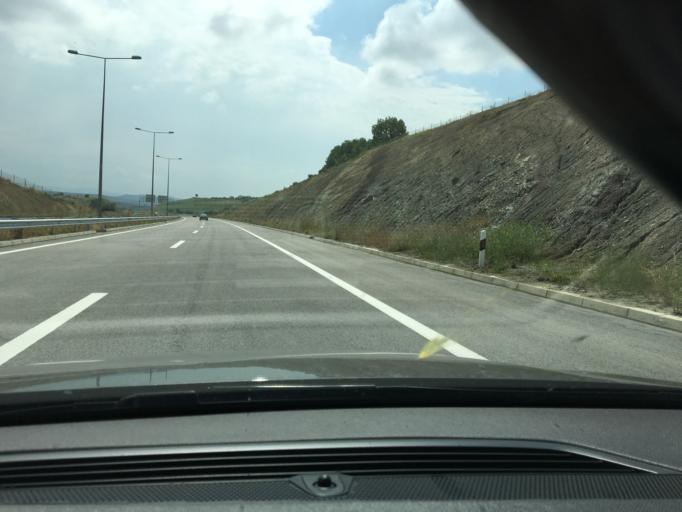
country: MK
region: Sveti Nikole
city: Gorobinci
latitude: 41.9157
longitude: 21.8810
